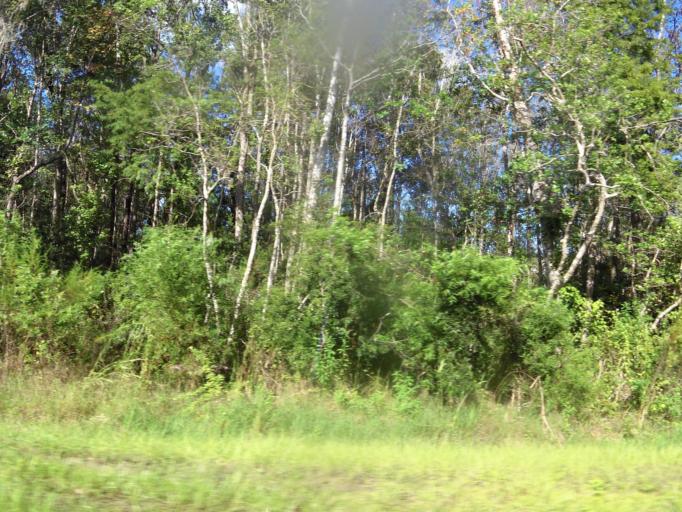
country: US
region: Florida
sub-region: Duval County
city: Jacksonville Beach
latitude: 30.2761
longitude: -81.5071
